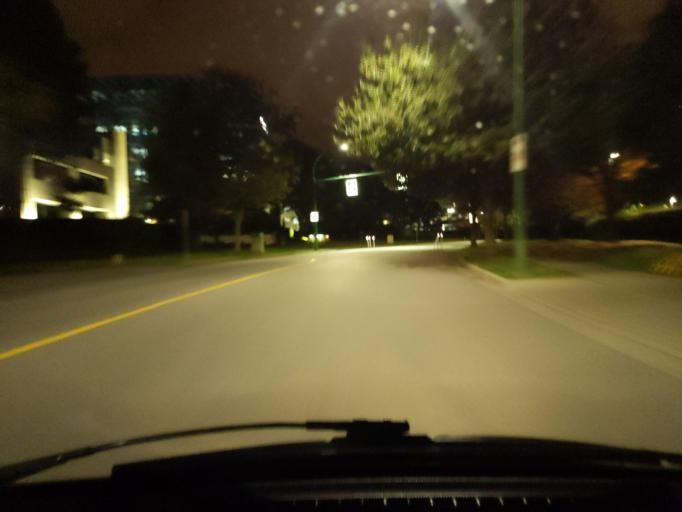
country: CA
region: British Columbia
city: Burnaby
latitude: 49.2591
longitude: -123.0094
